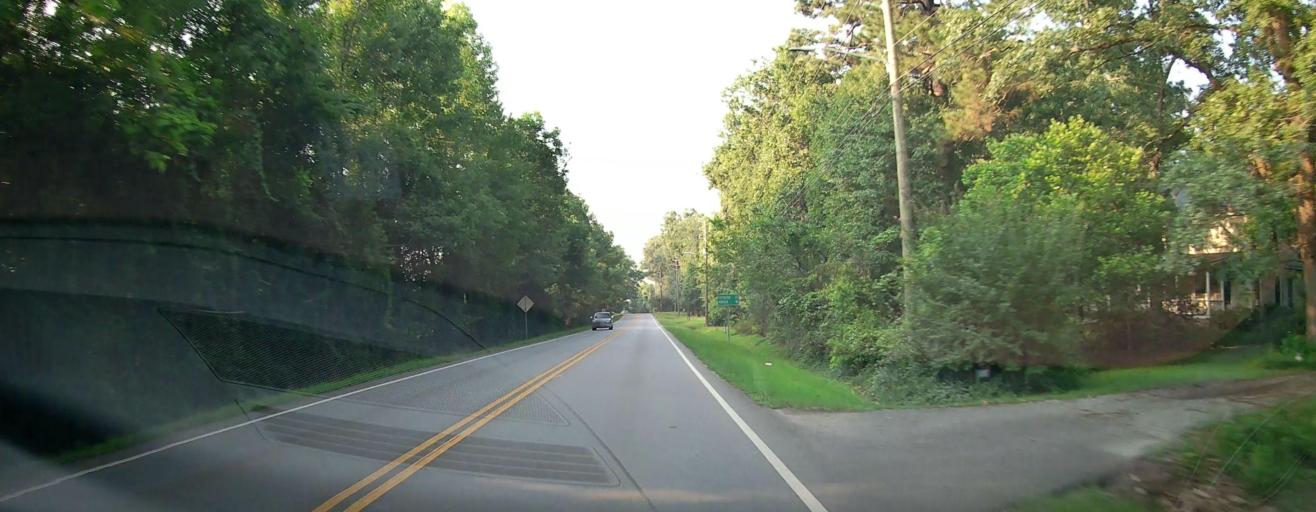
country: US
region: Georgia
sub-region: Jones County
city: Gray
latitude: 33.0113
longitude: -83.5335
